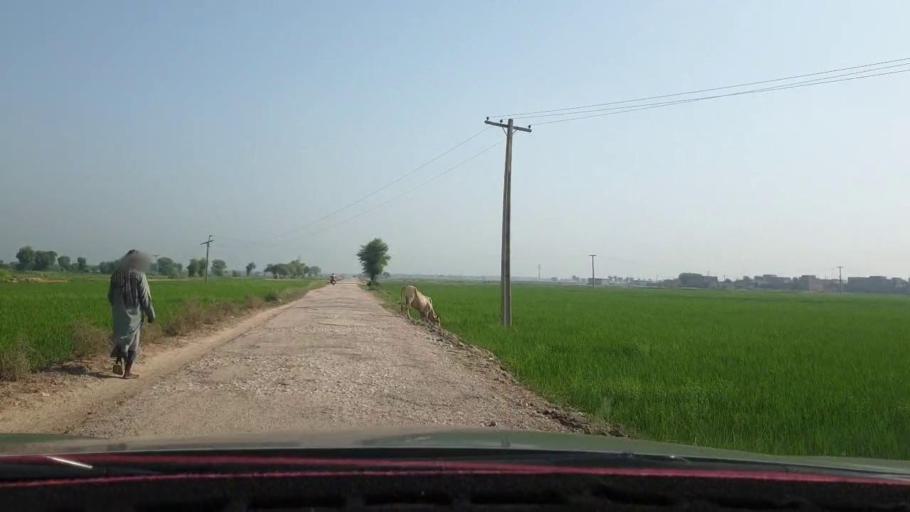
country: PK
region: Sindh
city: Nasirabad
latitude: 27.4922
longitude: 67.9282
